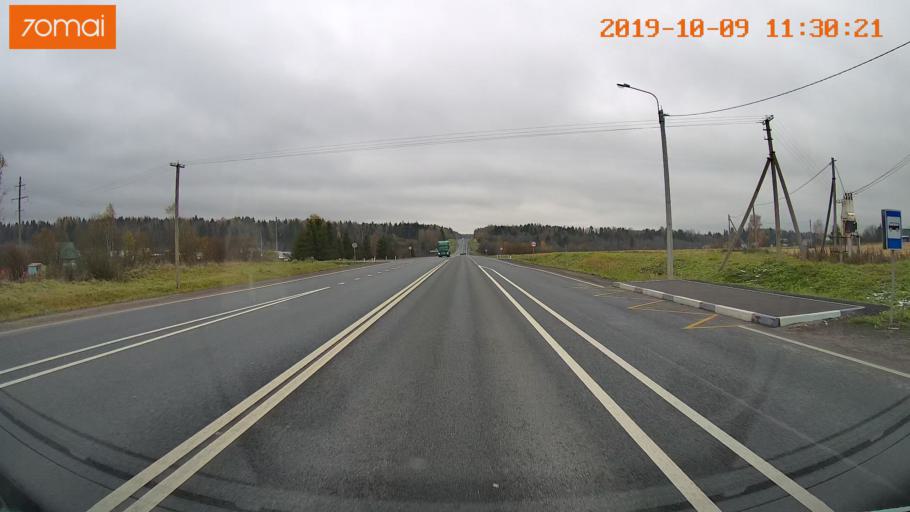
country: RU
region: Vologda
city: Gryazovets
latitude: 59.0545
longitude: 40.0733
